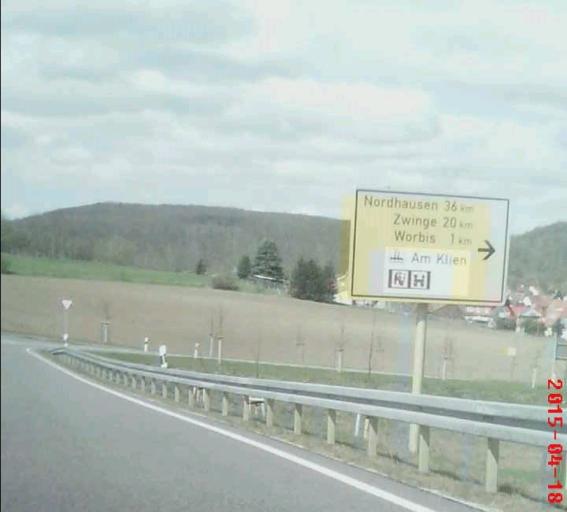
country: DE
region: Thuringia
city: Worbis
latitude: 51.4190
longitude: 10.3568
